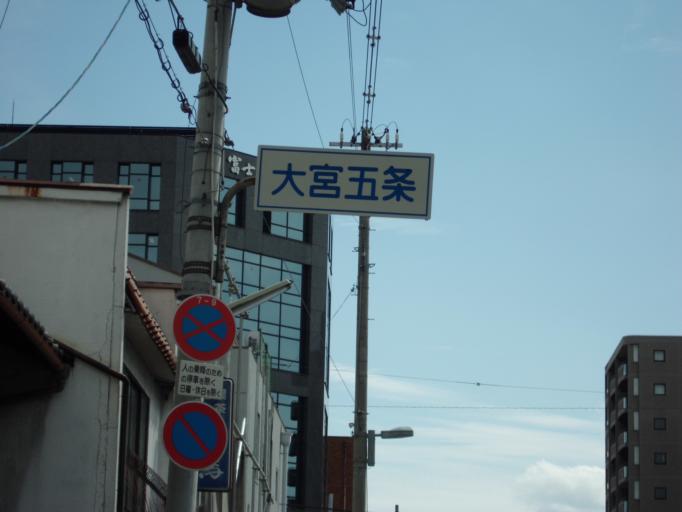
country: JP
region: Kyoto
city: Kyoto
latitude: 34.9969
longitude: 135.7491
